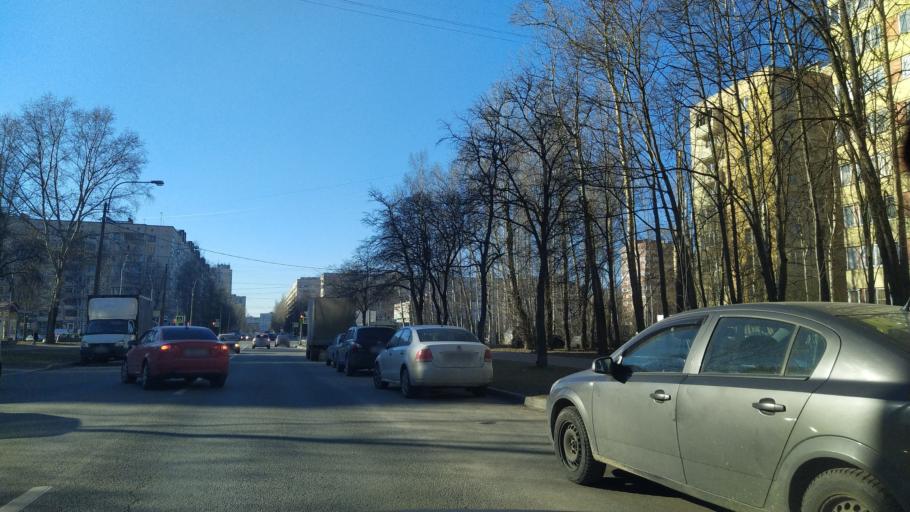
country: RU
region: St.-Petersburg
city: Grazhdanka
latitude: 60.0336
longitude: 30.3963
